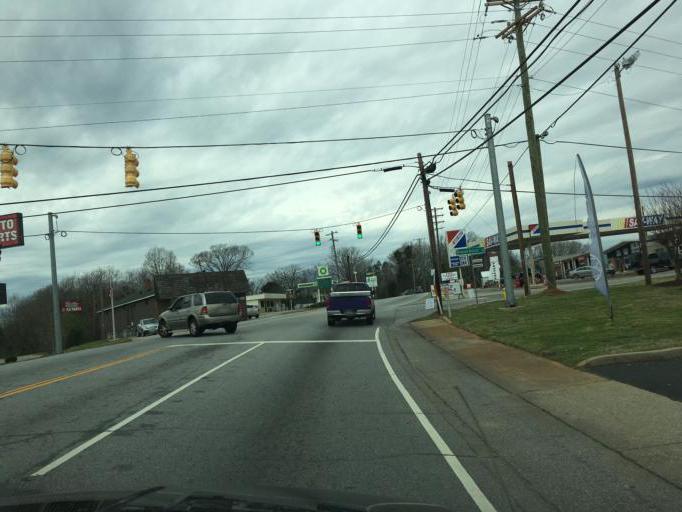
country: US
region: South Carolina
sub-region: Anderson County
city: Piedmont
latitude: 34.7013
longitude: -82.4772
